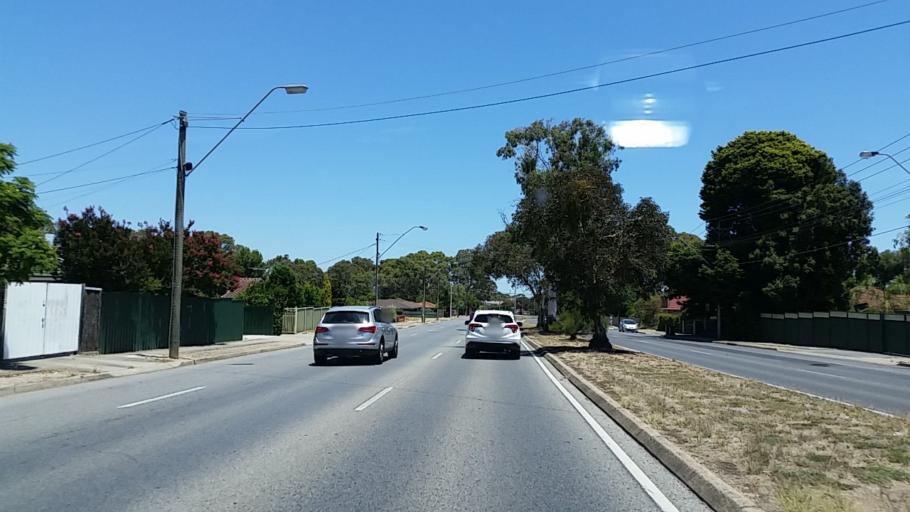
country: AU
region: South Australia
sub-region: Tea Tree Gully
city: Hope Valley
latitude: -34.8250
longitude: 138.7087
